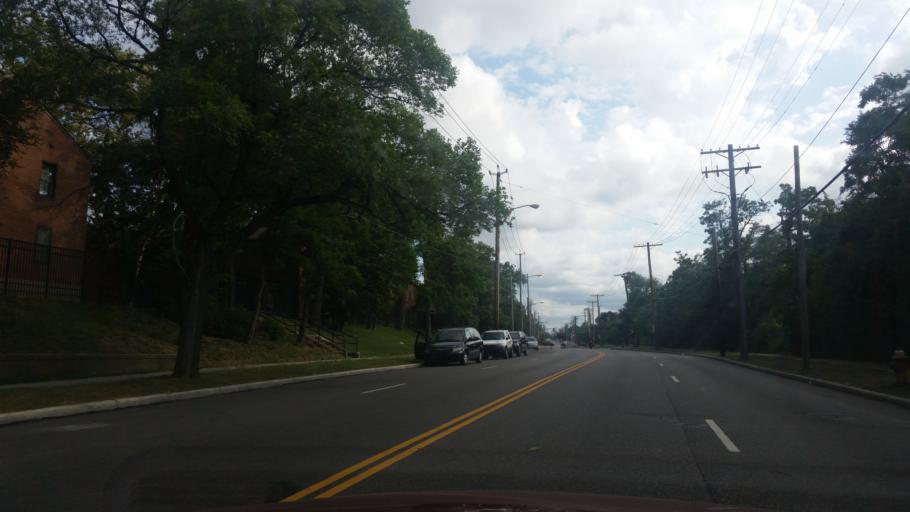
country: US
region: Ohio
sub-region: Cuyahoga County
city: Bratenahl
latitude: 41.4908
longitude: -81.6135
